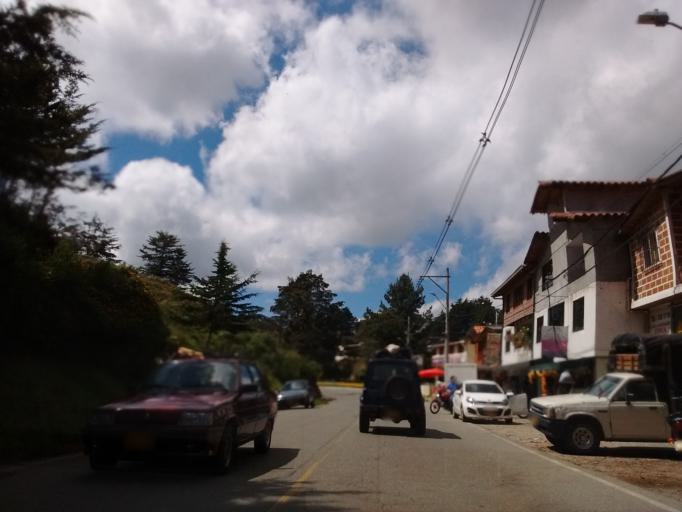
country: CO
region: Antioquia
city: Medellin
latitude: 6.2128
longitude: -75.5021
